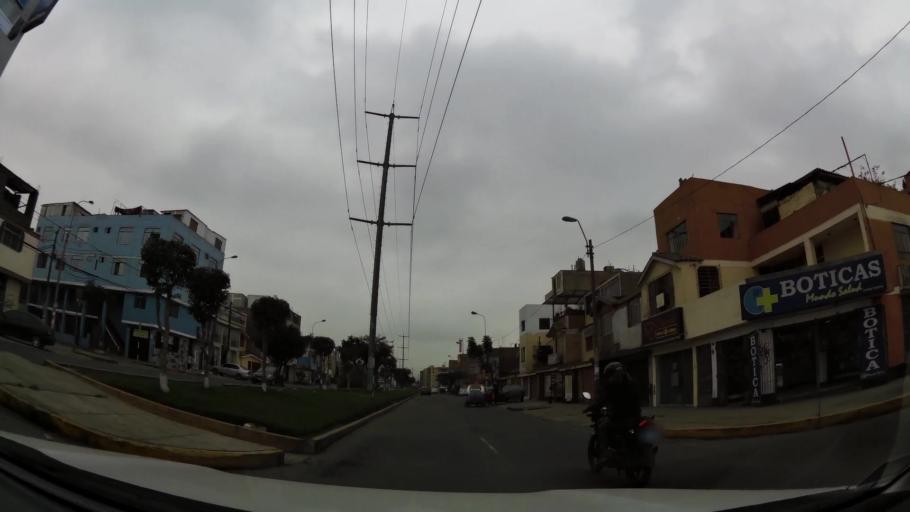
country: PE
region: Lima
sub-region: Lima
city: Vitarte
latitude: -12.0483
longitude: -76.9677
